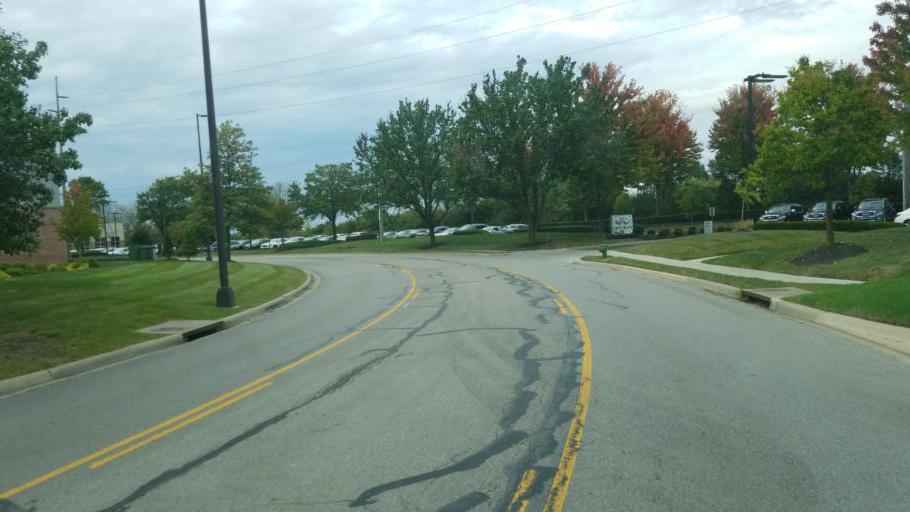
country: US
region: Ohio
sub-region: Franklin County
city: Dublin
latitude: 40.1072
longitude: -83.0926
